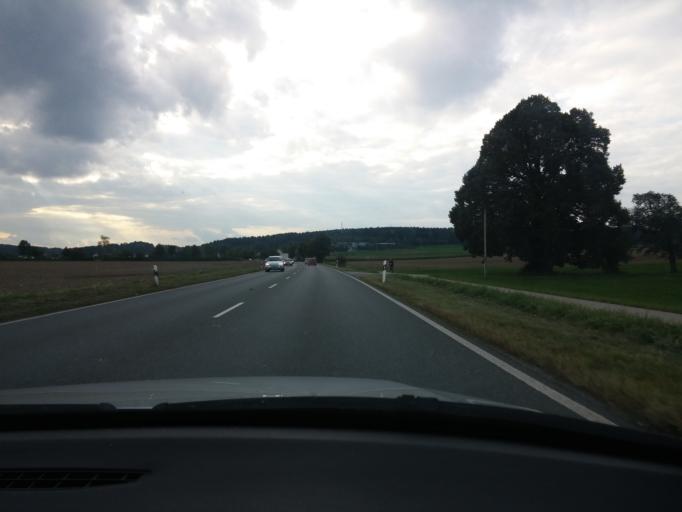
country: DE
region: Bavaria
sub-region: Upper Bavaria
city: Kirchseeon
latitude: 48.0688
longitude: 11.9229
